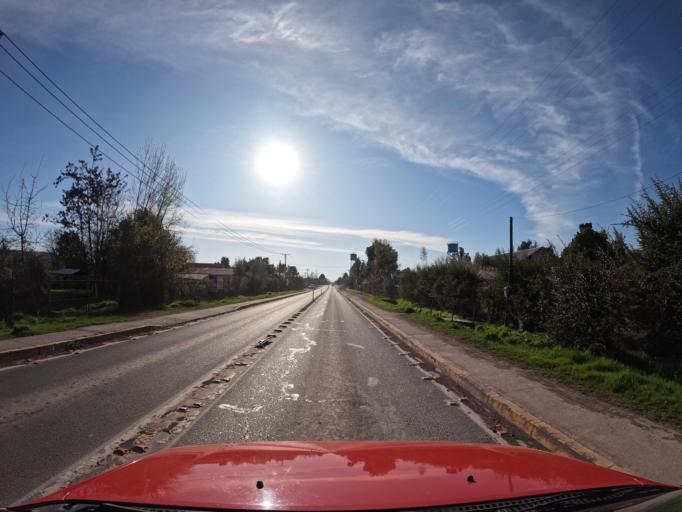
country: CL
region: Maule
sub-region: Provincia de Curico
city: Teno
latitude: -34.9600
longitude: -70.9709
